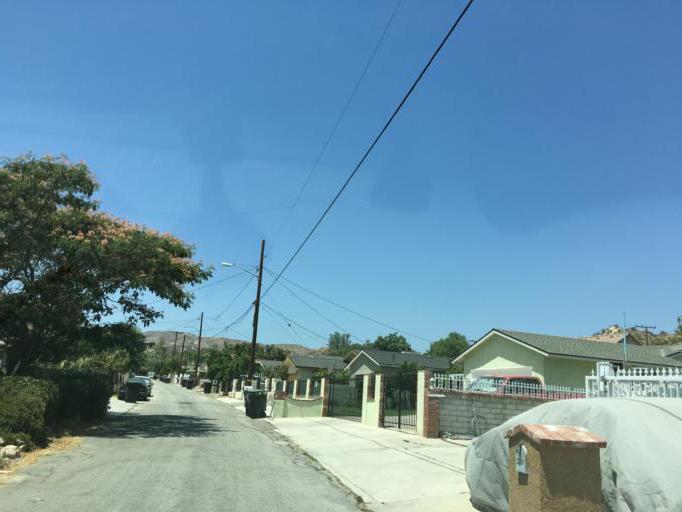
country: US
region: California
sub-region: Los Angeles County
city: Val Verde
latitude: 34.4474
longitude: -118.6671
